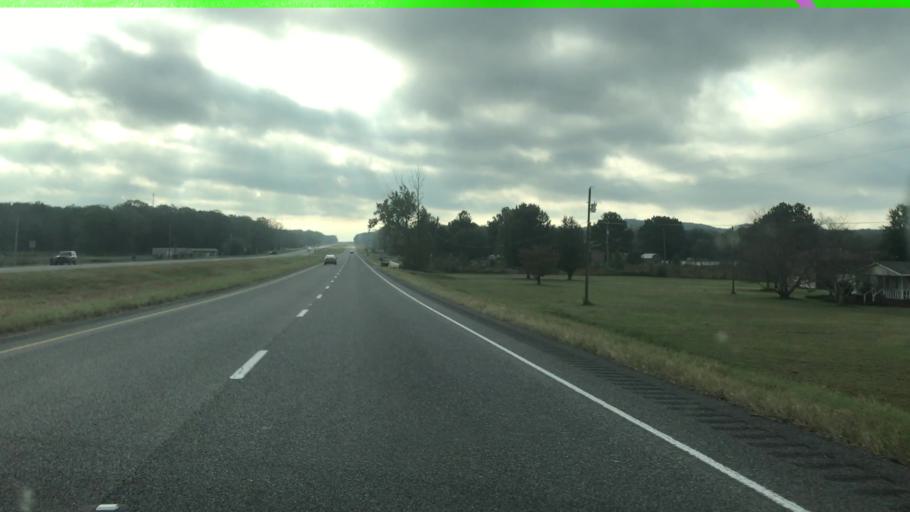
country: US
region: Alabama
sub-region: Morgan County
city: Danville
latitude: 34.4119
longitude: -87.1530
